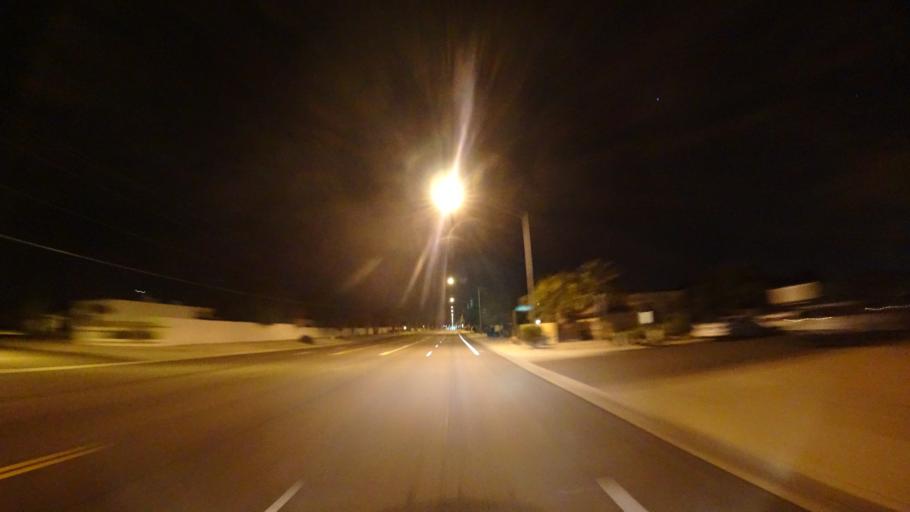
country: US
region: Arizona
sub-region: Maricopa County
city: Mesa
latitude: 33.4651
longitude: -111.7014
